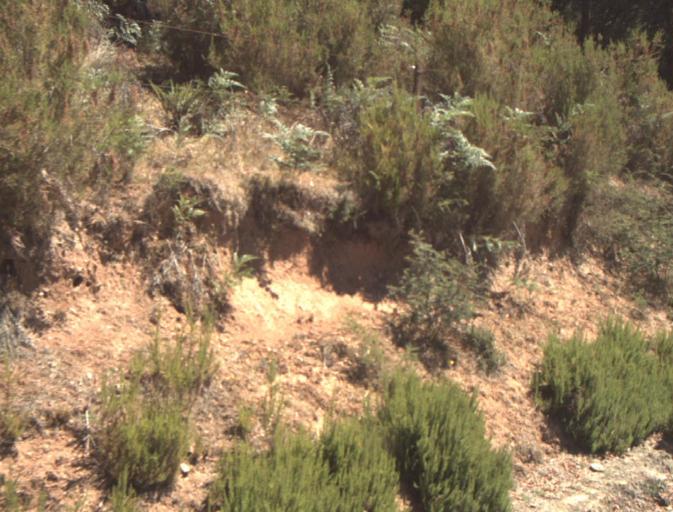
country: AU
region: Tasmania
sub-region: Dorset
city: Scottsdale
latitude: -41.3046
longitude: 147.3676
